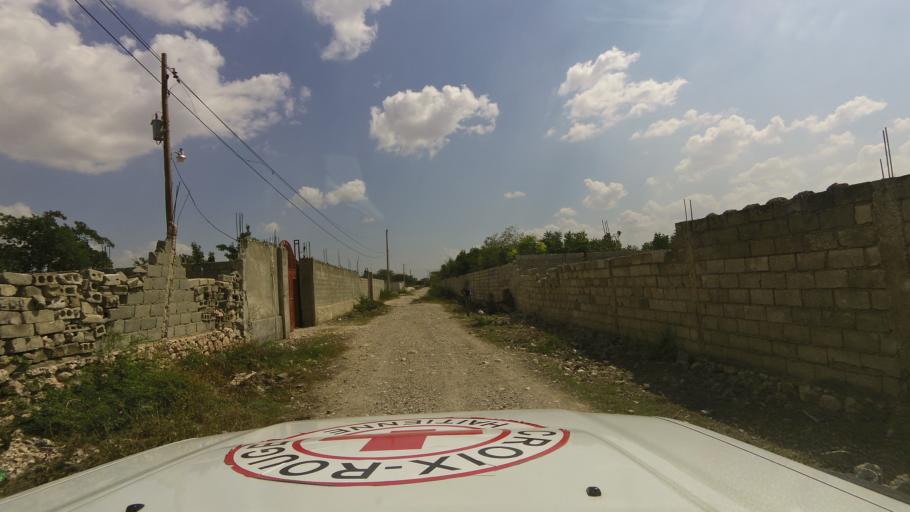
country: HT
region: Ouest
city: Croix des Bouquets
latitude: 18.6415
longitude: -72.2651
